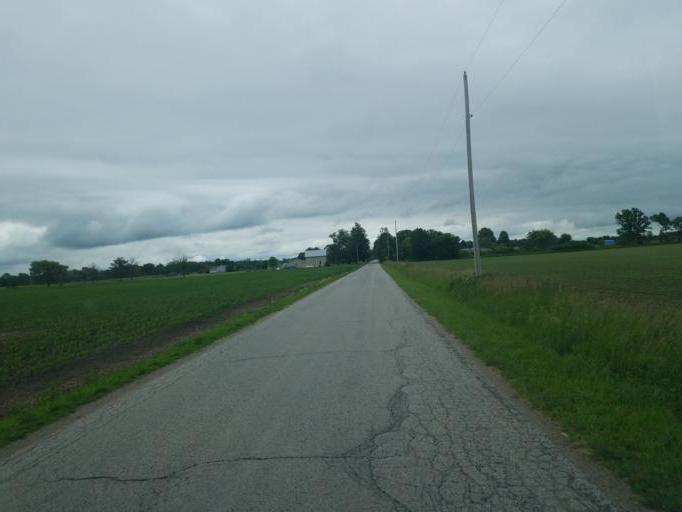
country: US
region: Ohio
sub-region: Morrow County
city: Cardington
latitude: 40.5279
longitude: -82.8875
